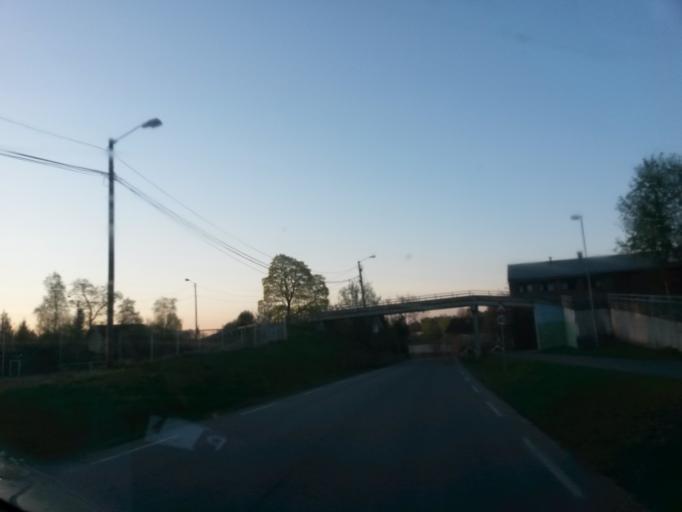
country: NO
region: Akershus
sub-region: Asker
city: Asker
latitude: 59.8299
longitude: 10.4028
